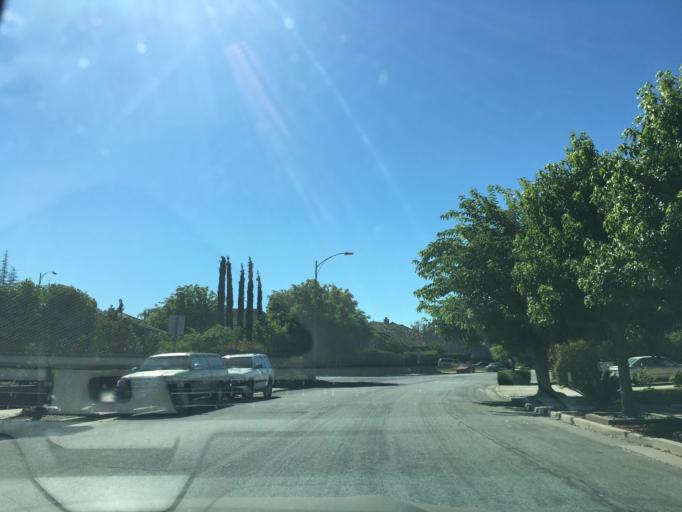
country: US
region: California
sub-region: Santa Clara County
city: Seven Trees
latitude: 37.2441
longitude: -121.8627
